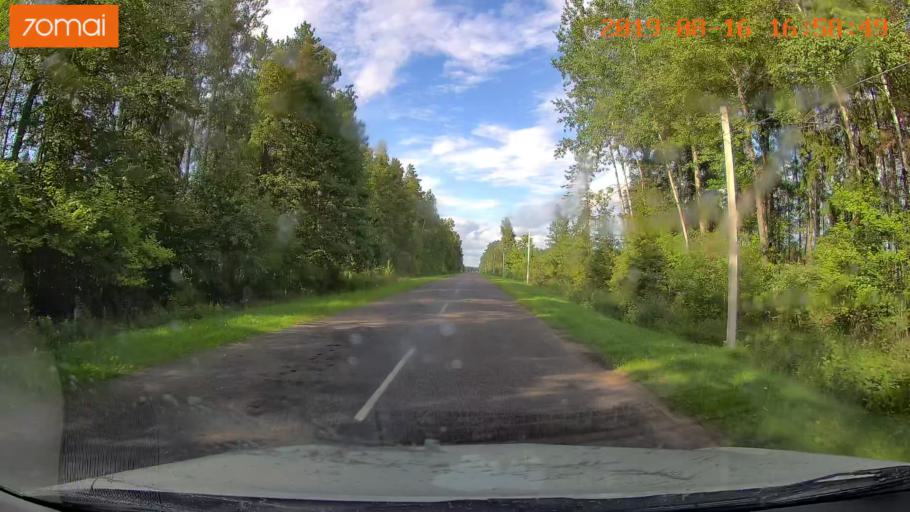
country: BY
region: Mogilev
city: Hlusha
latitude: 53.2745
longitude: 28.8367
